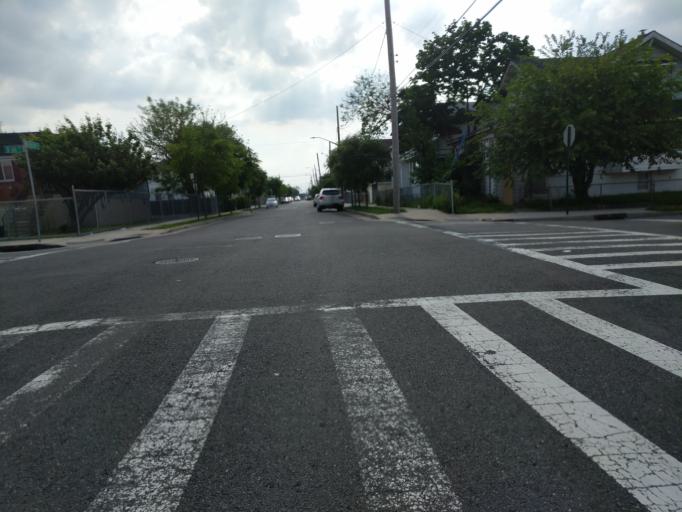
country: US
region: New York
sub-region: Nassau County
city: Inwood
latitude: 40.5950
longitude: -73.7952
